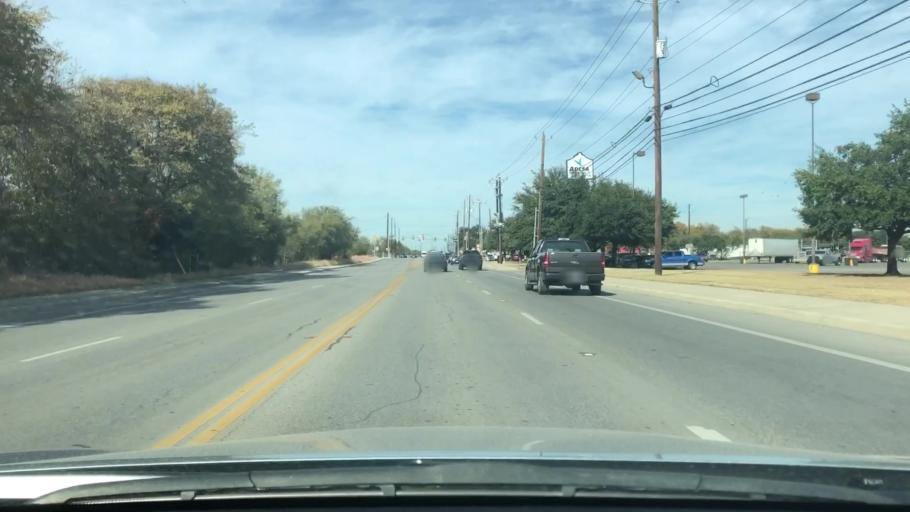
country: US
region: Texas
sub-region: Bexar County
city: Lackland Air Force Base
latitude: 29.4328
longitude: -98.5997
